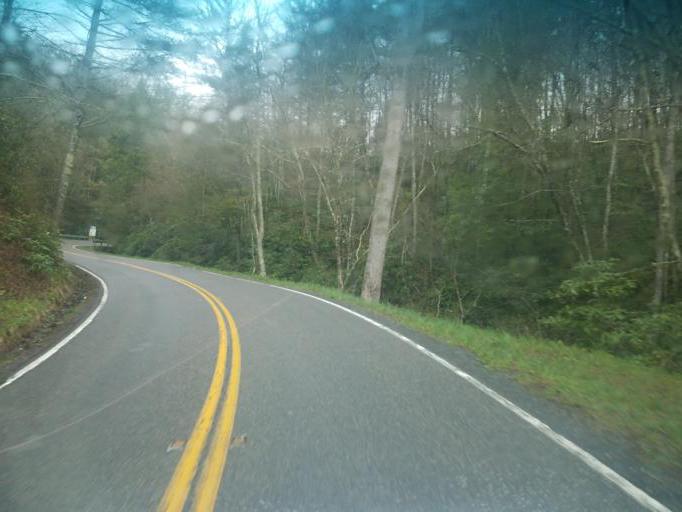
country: US
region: Virginia
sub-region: Smyth County
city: Chilhowie
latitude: 36.6482
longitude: -81.7070
